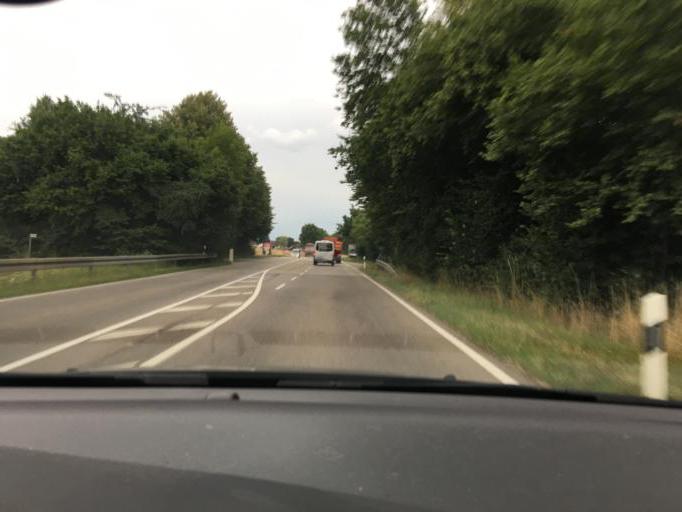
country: DE
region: Bavaria
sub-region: Upper Bavaria
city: Erding
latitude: 48.2996
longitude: 11.9149
